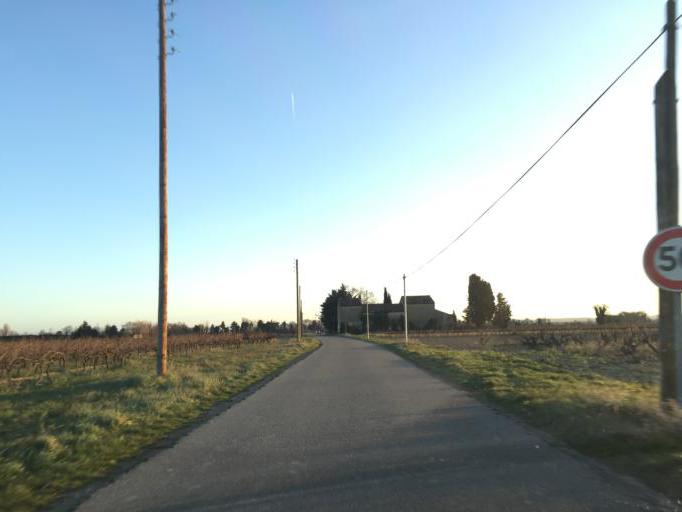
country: FR
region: Provence-Alpes-Cote d'Azur
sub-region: Departement du Vaucluse
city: Camaret-sur-Aigues
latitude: 44.1487
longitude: 4.8745
